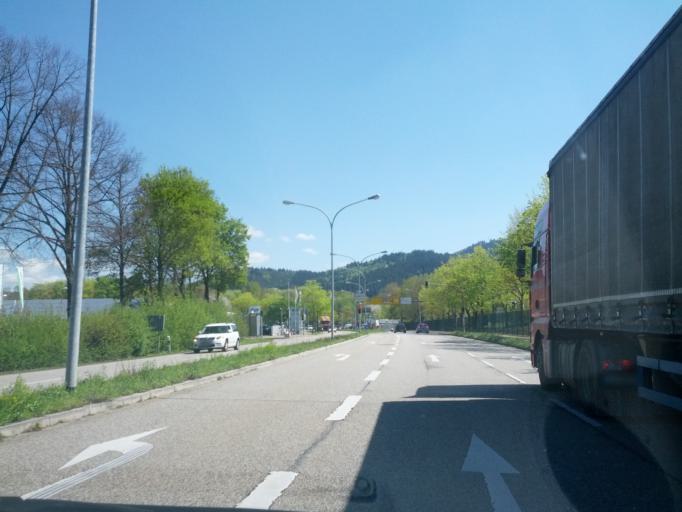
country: DE
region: Baden-Wuerttemberg
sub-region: Freiburg Region
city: Gundelfingen
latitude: 48.0343
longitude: 7.8567
